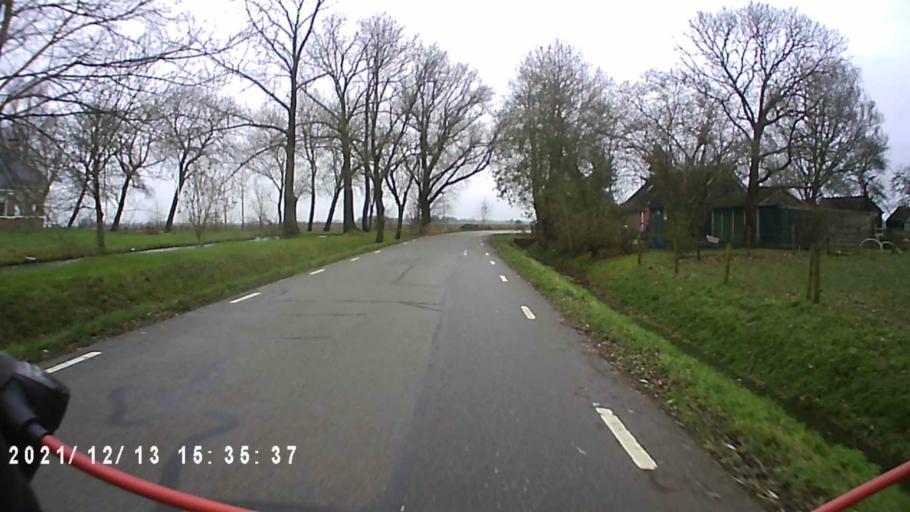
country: NL
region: Groningen
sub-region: Gemeente Appingedam
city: Appingedam
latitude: 53.3305
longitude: 6.8260
